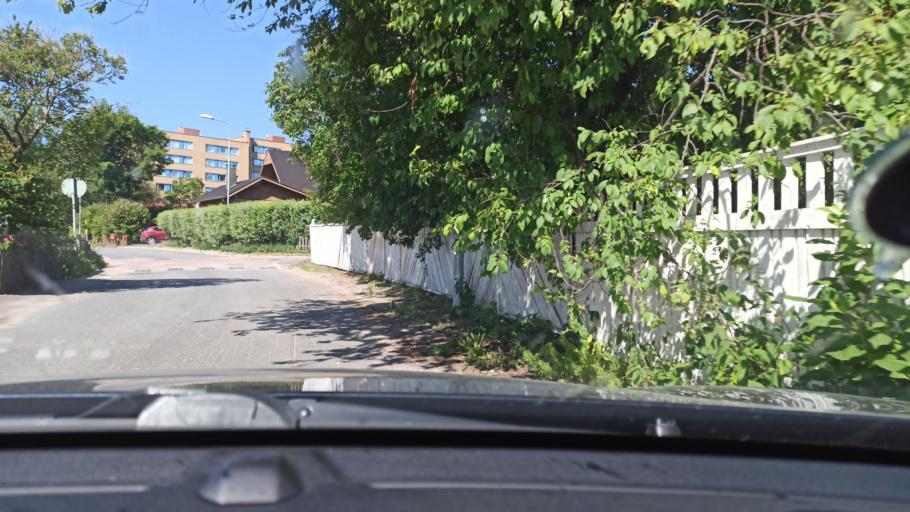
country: FI
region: Northern Ostrobothnia
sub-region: Oulu
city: Oulu
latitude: 65.0410
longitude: 25.4432
